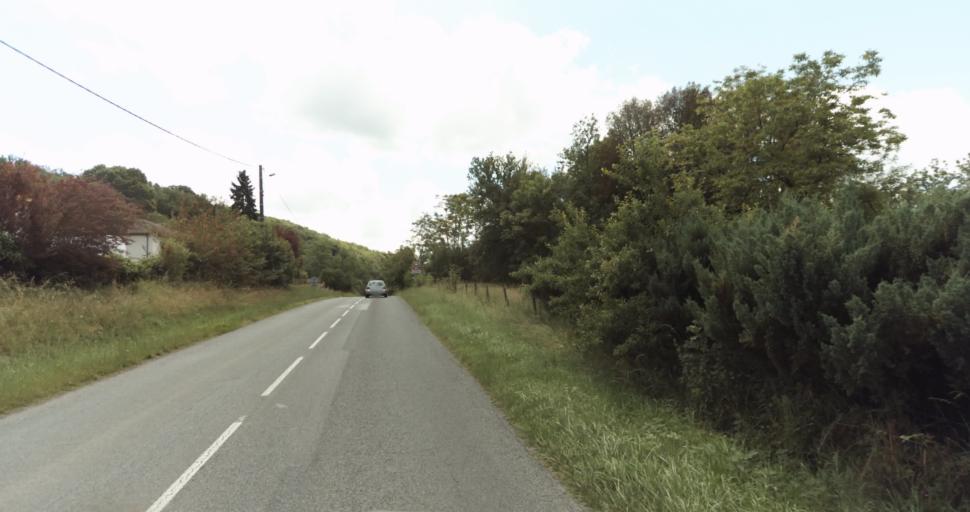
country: FR
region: Aquitaine
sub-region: Departement de la Dordogne
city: Lalinde
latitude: 44.8197
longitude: 0.7078
